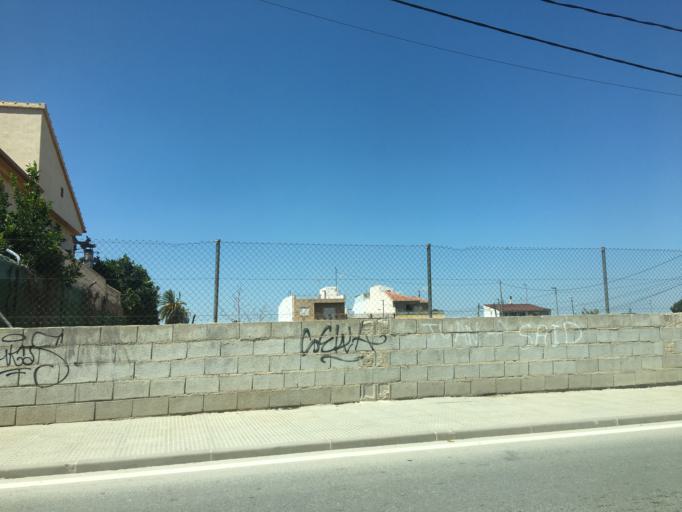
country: ES
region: Murcia
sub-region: Murcia
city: Murcia
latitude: 38.0078
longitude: -1.1146
